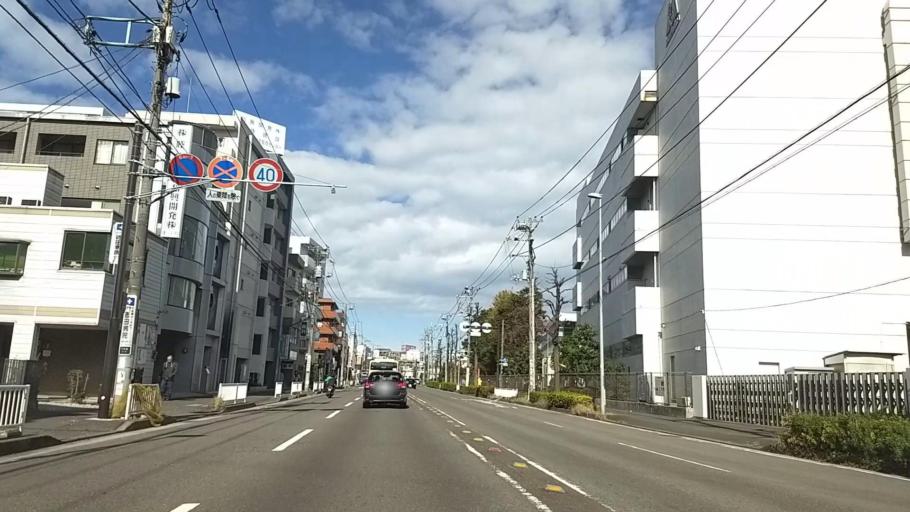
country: JP
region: Kanagawa
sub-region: Kawasaki-shi
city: Kawasaki
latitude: 35.5166
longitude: 139.6736
